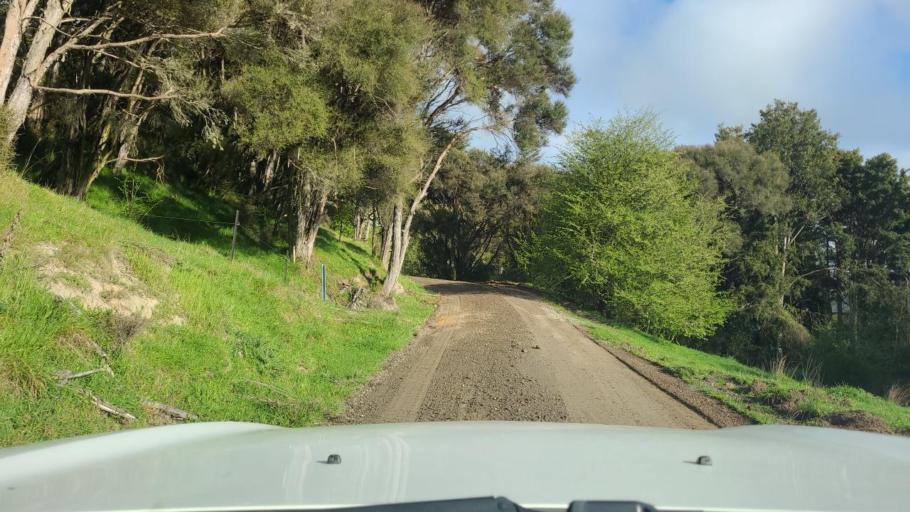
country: NZ
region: Wellington
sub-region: South Wairarapa District
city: Waipawa
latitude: -41.2310
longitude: 175.6827
